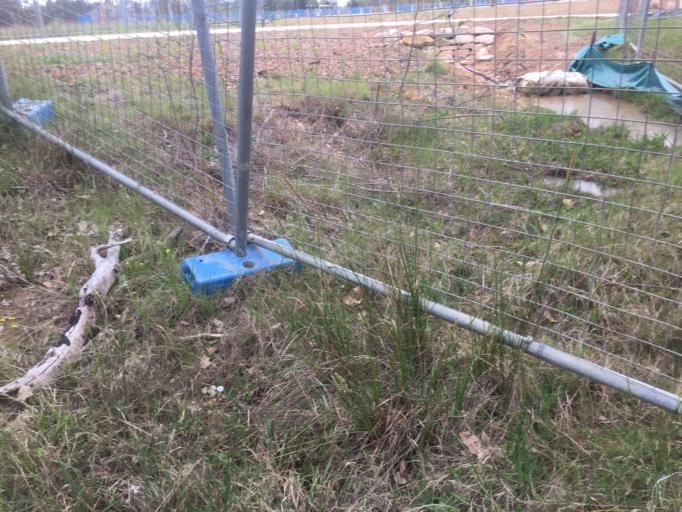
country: AU
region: New South Wales
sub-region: Blacktown
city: Doonside
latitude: -33.7850
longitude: 150.8695
